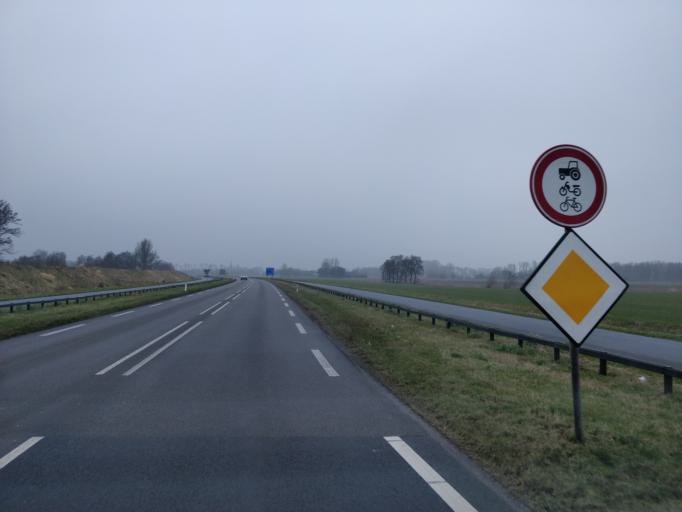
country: NL
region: Friesland
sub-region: Menameradiel
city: Marsum
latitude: 53.2264
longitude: 5.6987
